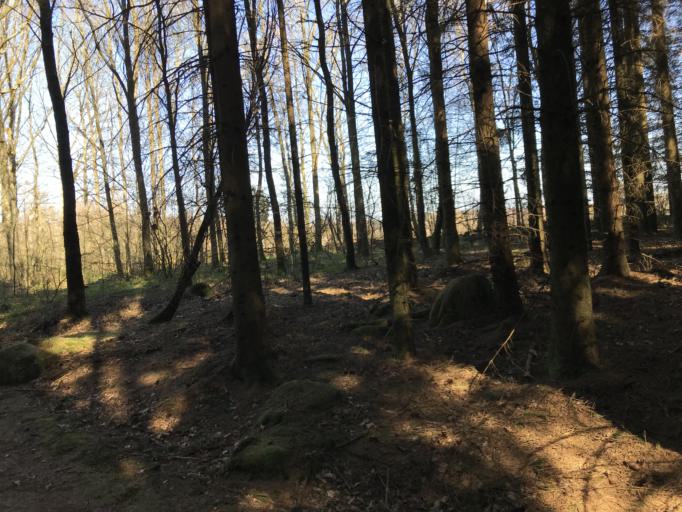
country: SE
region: Skane
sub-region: Eslovs Kommun
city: Stehag
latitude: 56.0104
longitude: 13.3799
